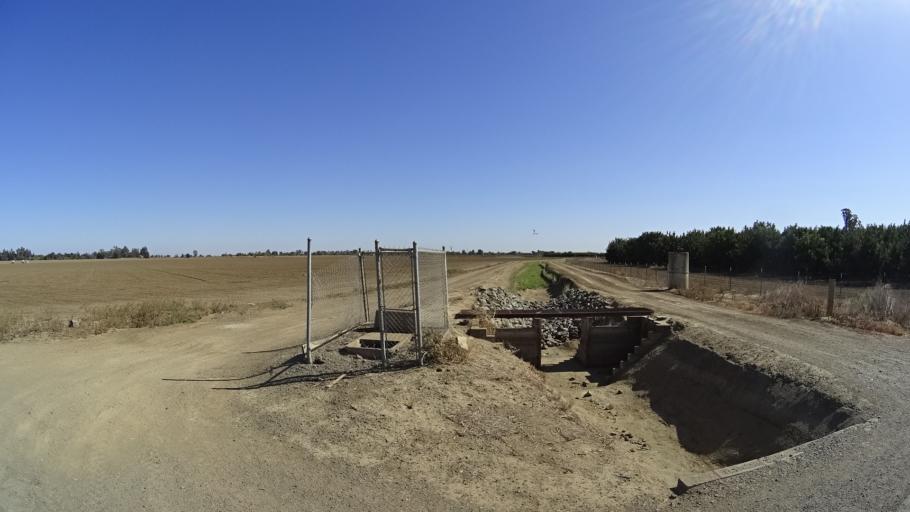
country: US
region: California
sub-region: Solano County
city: Dixon
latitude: 38.5509
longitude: -121.8588
